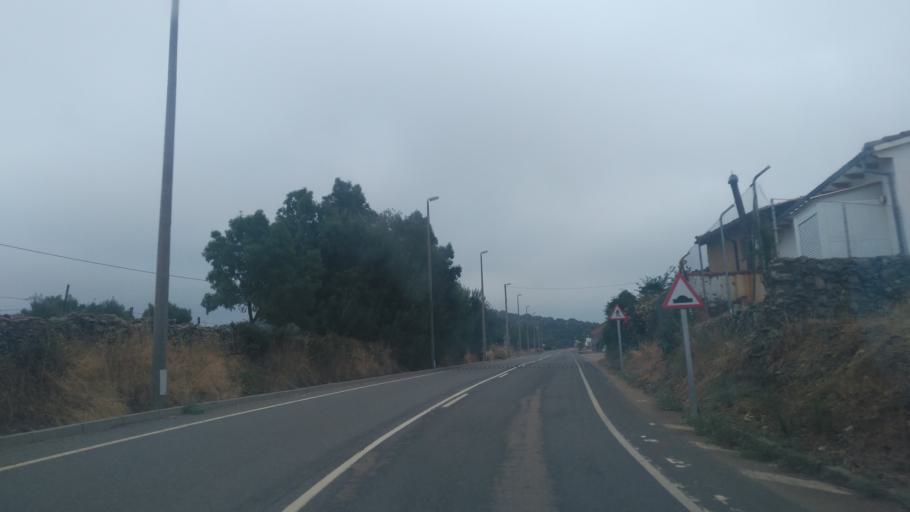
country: ES
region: Castille and Leon
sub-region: Provincia de Salamanca
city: Aldeanueva de la Sierra
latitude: 40.6162
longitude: -6.0991
